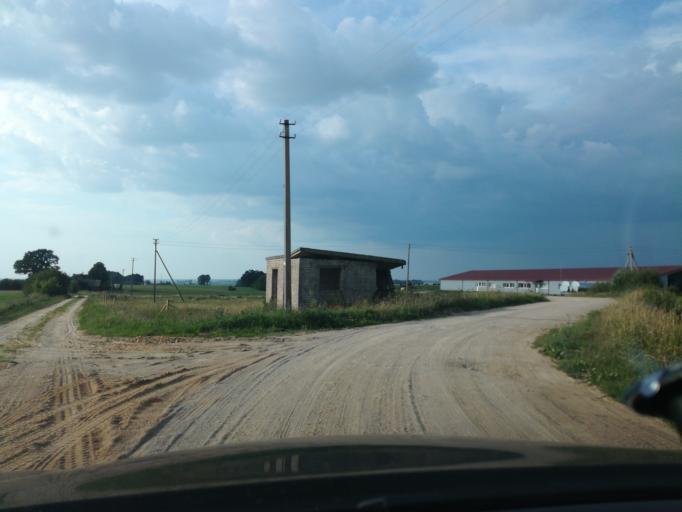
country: LT
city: Simnas
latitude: 54.3919
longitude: 23.8162
